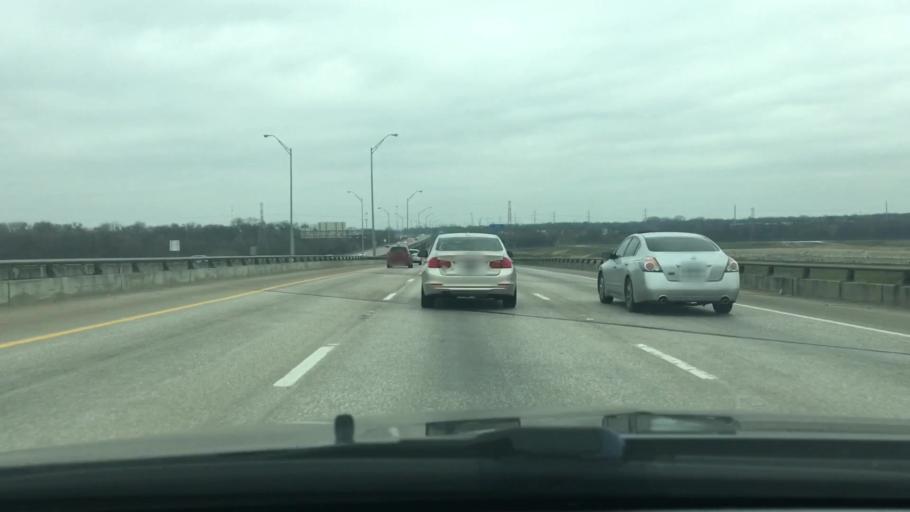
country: US
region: Texas
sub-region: Dallas County
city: Dallas
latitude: 32.7337
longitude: -96.7667
